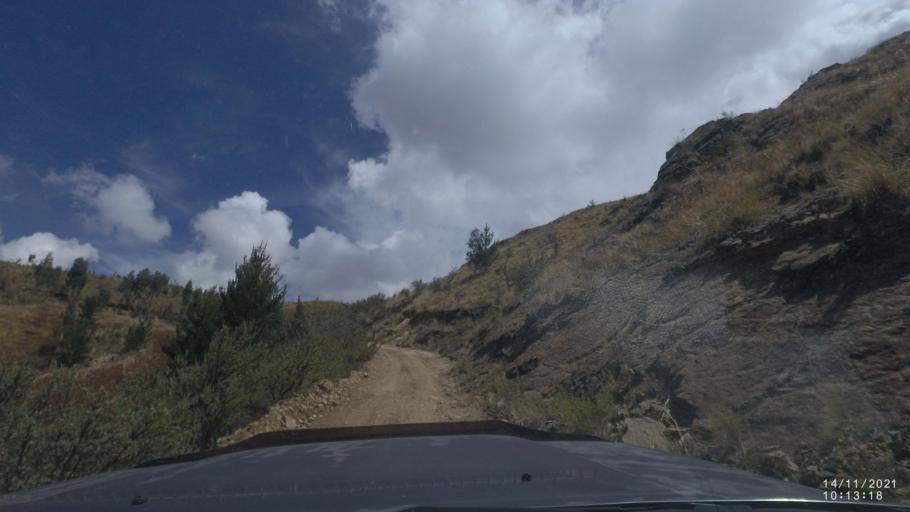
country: BO
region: Cochabamba
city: Cochabamba
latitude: -17.3439
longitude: -66.0863
